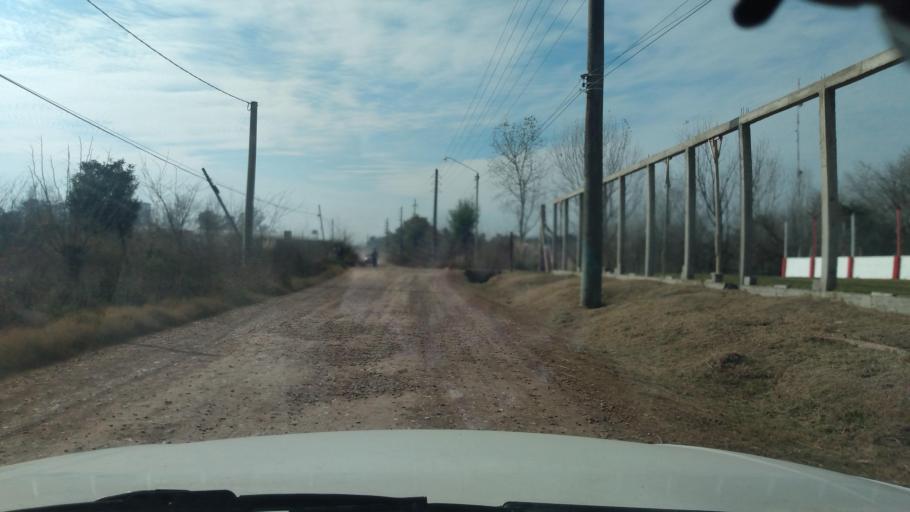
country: AR
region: Buenos Aires
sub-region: Partido de Lujan
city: Lujan
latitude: -34.5867
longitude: -59.1230
